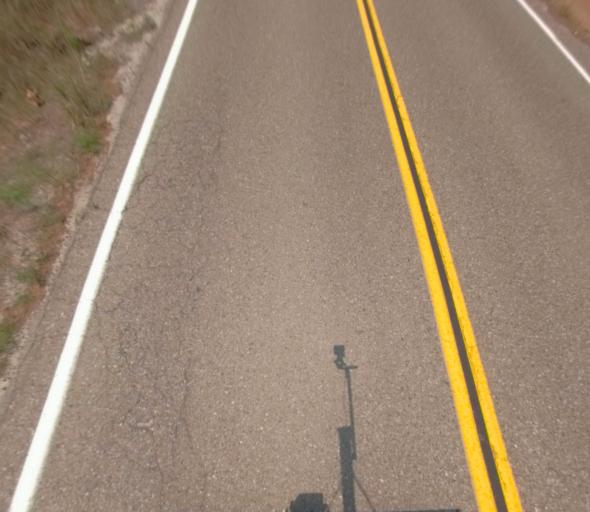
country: US
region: California
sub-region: Madera County
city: Oakhurst
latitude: 37.2599
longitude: -119.5713
